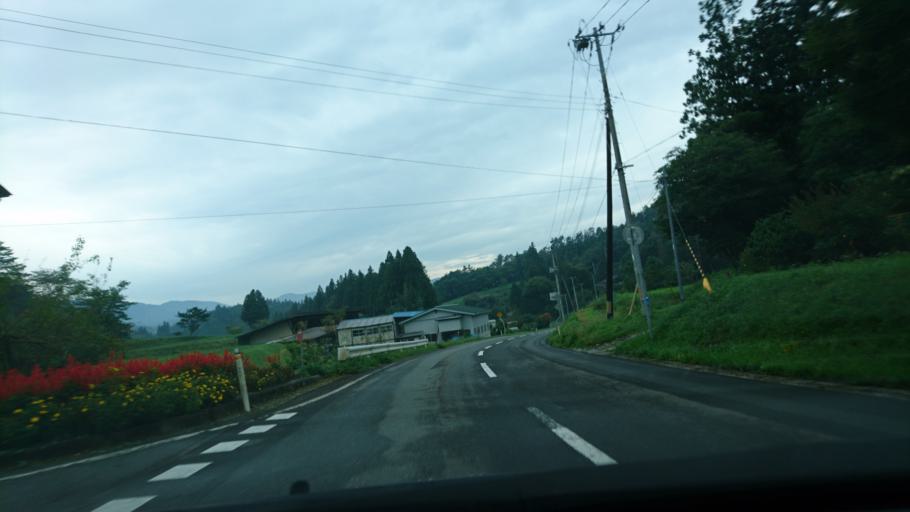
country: JP
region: Iwate
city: Ichinoseki
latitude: 39.0158
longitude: 141.2528
